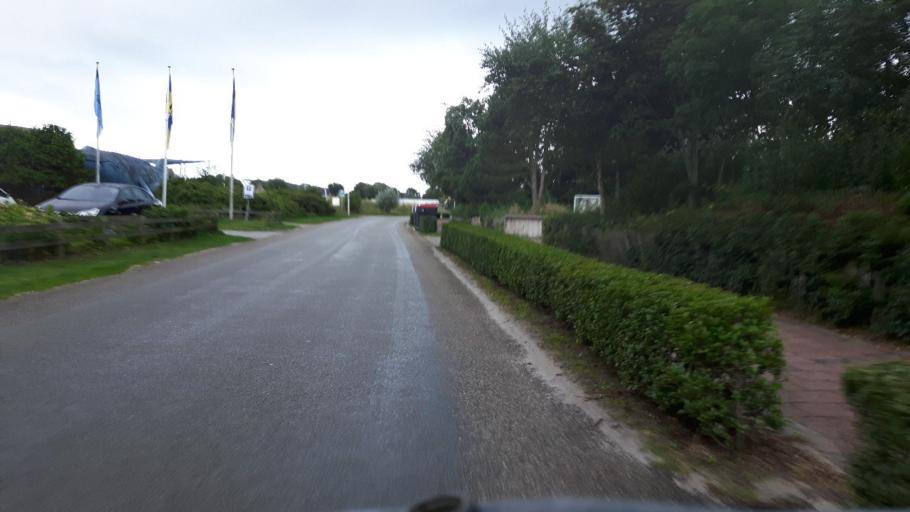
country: NL
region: Friesland
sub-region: Gemeente Ameland
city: Nes
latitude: 53.4509
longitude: 5.7752
